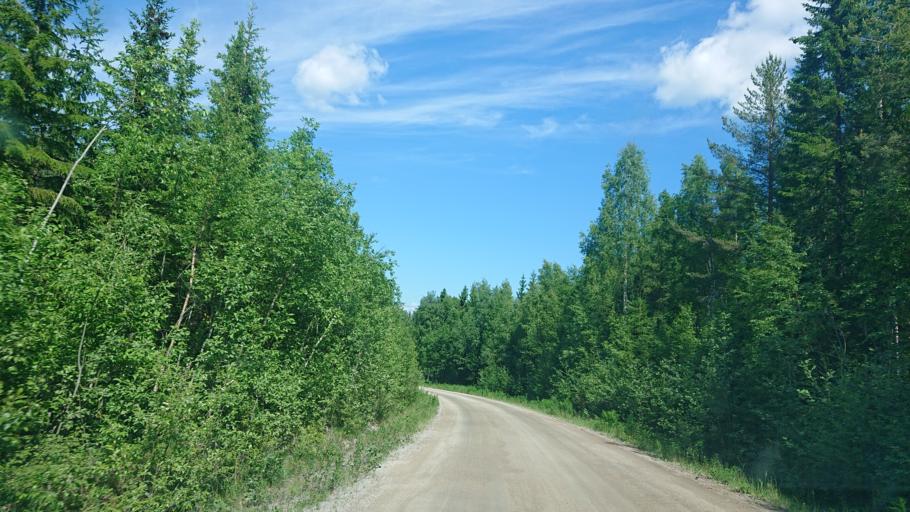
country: SE
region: Vaesternorrland
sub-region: Solleftea Kommun
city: Solleftea
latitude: 62.9683
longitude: 17.1589
